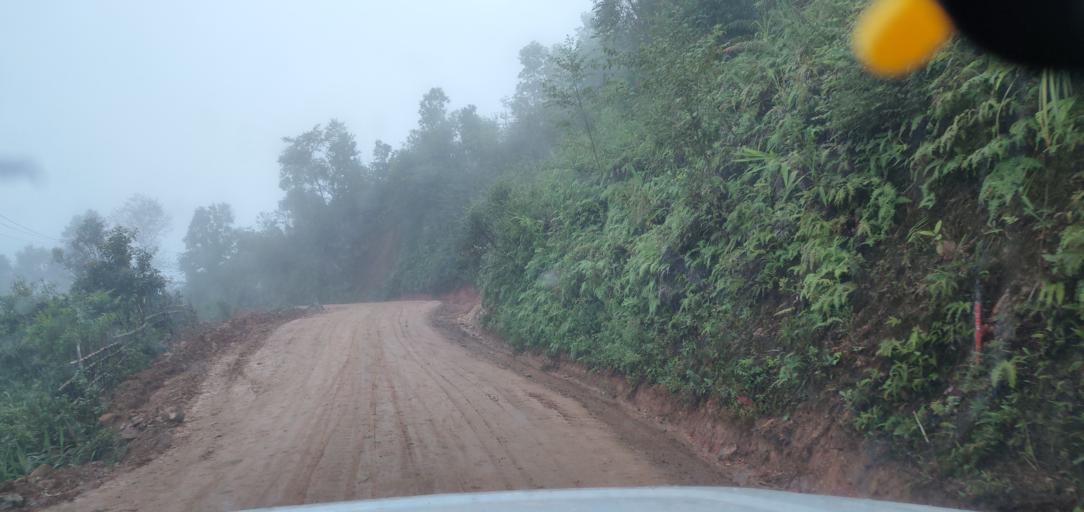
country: LA
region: Phongsali
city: Phongsali
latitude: 21.4289
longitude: 102.2599
